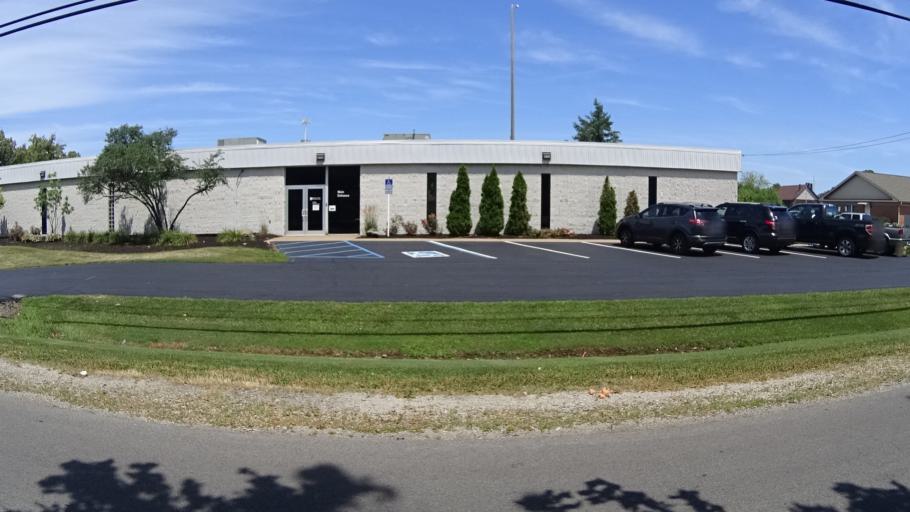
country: US
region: Ohio
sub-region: Erie County
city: Sandusky
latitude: 41.4378
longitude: -82.7165
